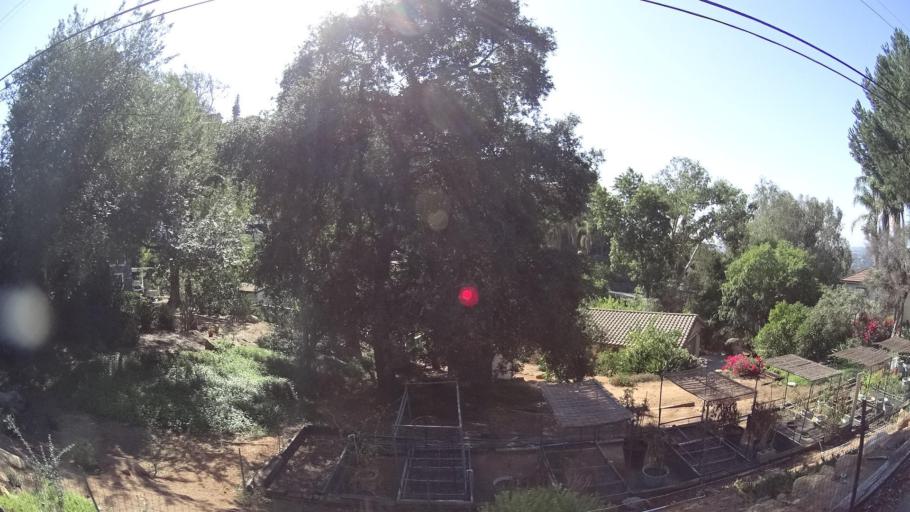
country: US
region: California
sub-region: San Diego County
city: Casa de Oro-Mount Helix
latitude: 32.7752
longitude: -116.9929
